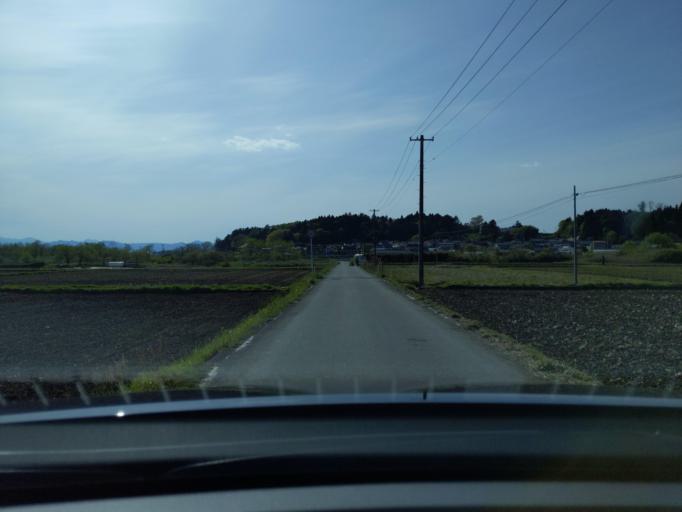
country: JP
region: Fukushima
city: Sukagawa
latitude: 37.2998
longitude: 140.4071
